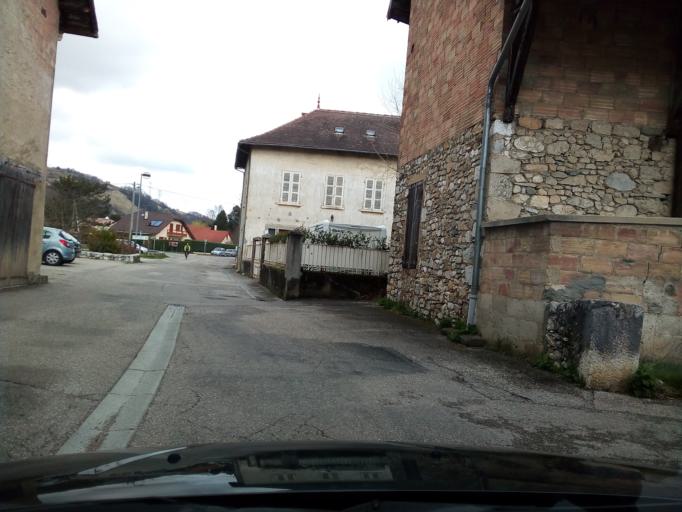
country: FR
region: Rhone-Alpes
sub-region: Departement de l'Isere
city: Chapareillan
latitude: 45.4706
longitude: 5.9869
